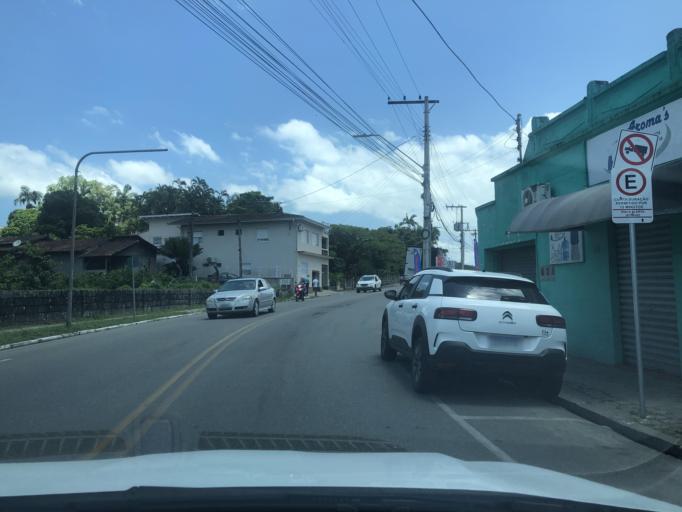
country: BR
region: Santa Catarina
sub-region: Sao Francisco Do Sul
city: Sao Francisco do Sul
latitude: -26.2513
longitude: -48.6416
